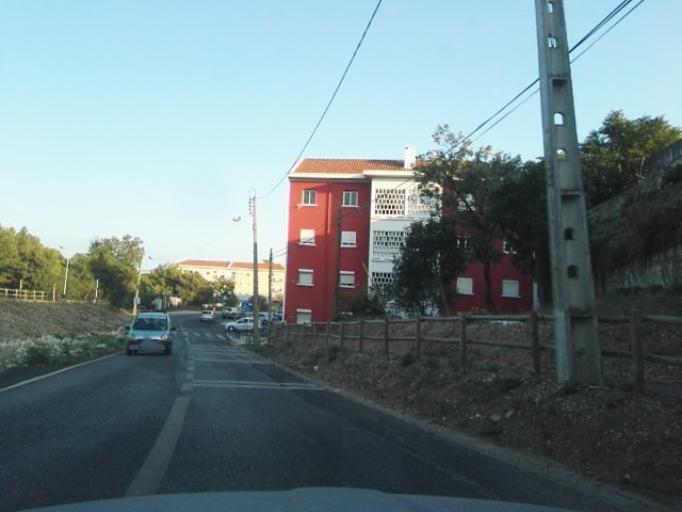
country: PT
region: Setubal
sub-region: Almada
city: Pragal
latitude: 38.7103
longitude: -9.1804
